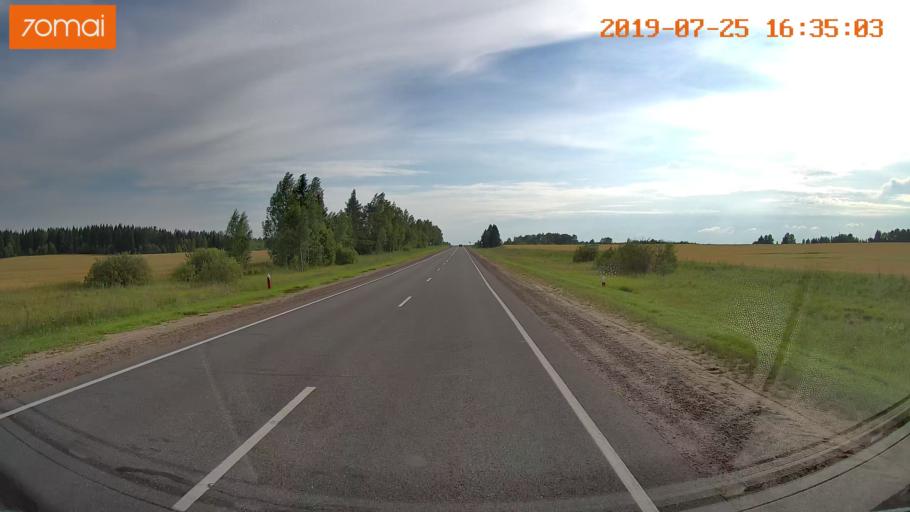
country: RU
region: Ivanovo
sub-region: Privolzhskiy Rayon
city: Ples
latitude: 57.4103
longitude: 41.4265
